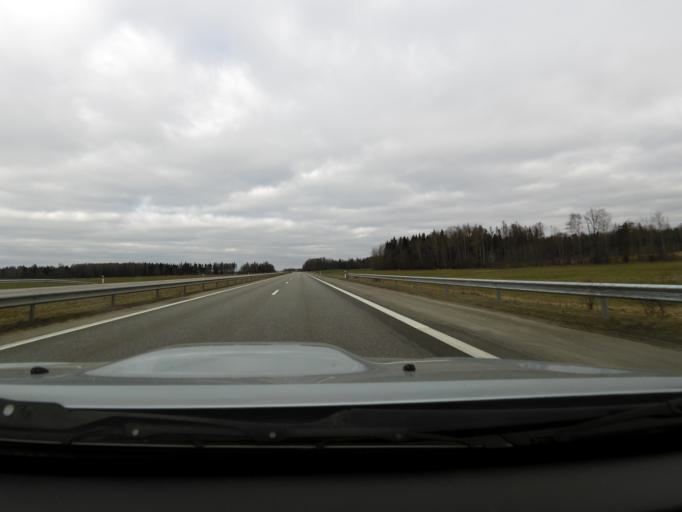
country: LT
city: Sirvintos
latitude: 55.0458
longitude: 24.8949
